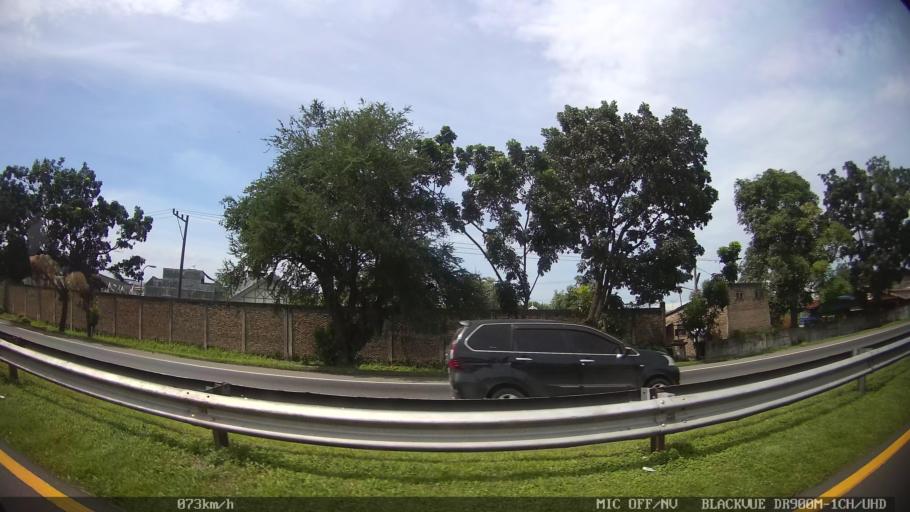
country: ID
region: North Sumatra
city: Medan
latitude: 3.6442
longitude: 98.6906
